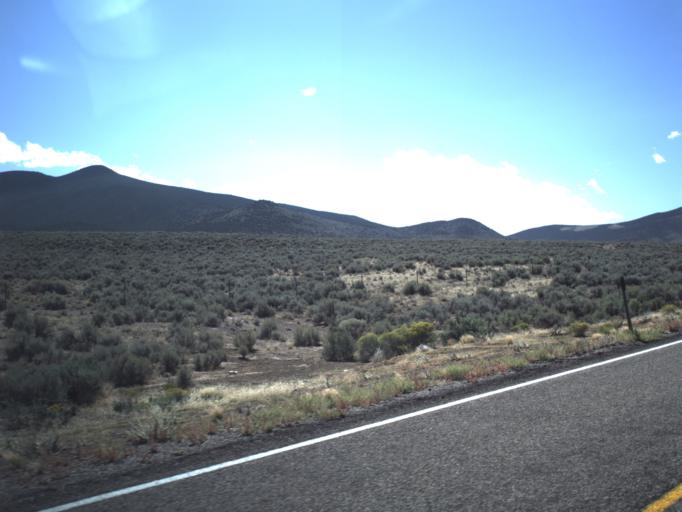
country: US
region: Utah
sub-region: Beaver County
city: Milford
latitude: 38.1812
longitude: -112.9449
